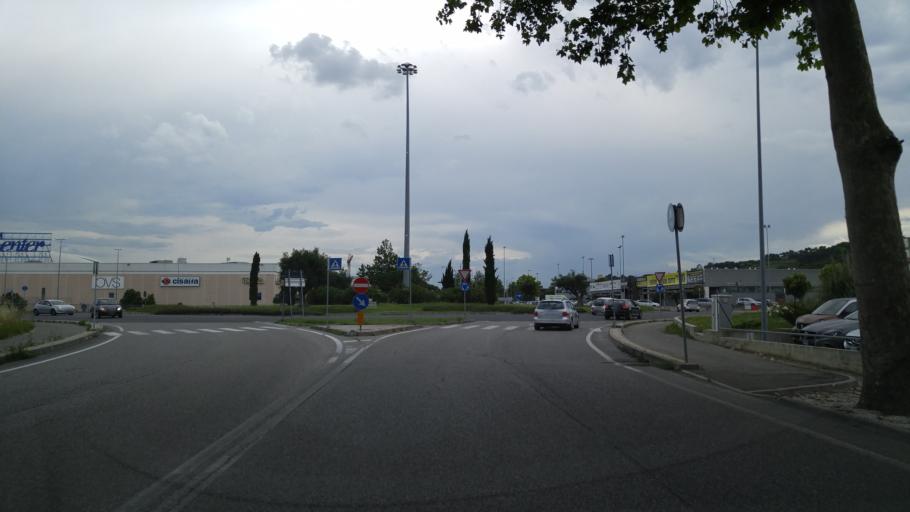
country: IT
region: The Marches
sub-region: Provincia di Pesaro e Urbino
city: Pesaro
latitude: 43.9069
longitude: 12.8709
